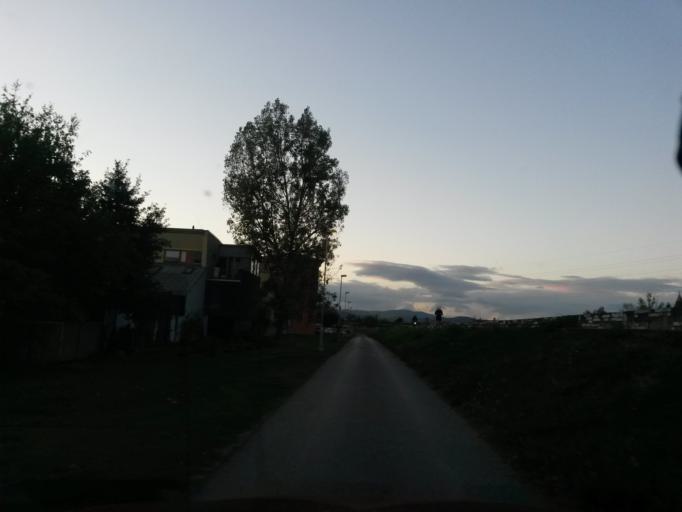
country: SK
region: Kosicky
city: Kosice
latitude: 48.6962
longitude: 21.2860
